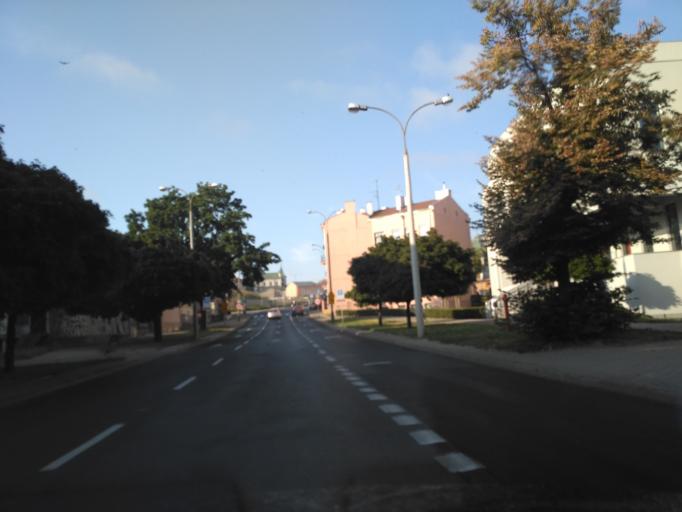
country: PL
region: Lublin Voivodeship
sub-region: Powiat lubelski
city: Lublin
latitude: 51.2510
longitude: 22.5665
